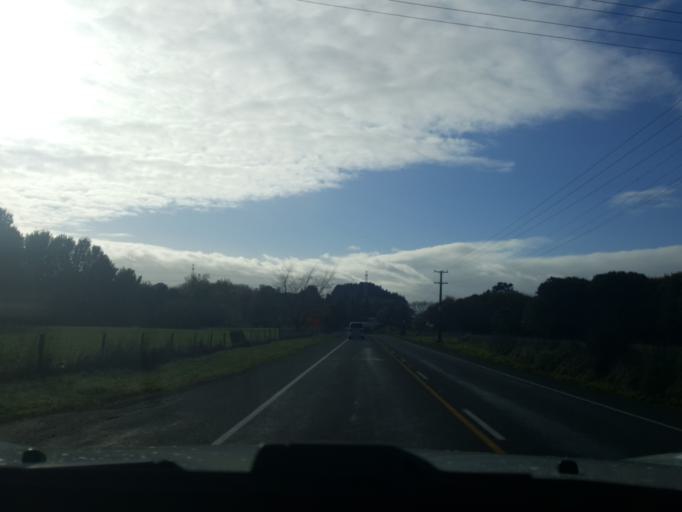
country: NZ
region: Waikato
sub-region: Waipa District
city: Cambridge
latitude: -37.6663
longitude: 175.4954
